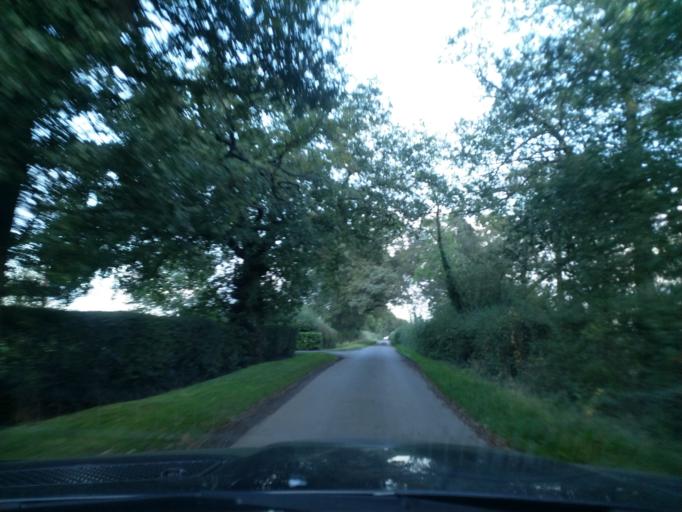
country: GB
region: England
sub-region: Warwickshire
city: Wroxall
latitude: 52.3470
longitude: -1.6631
